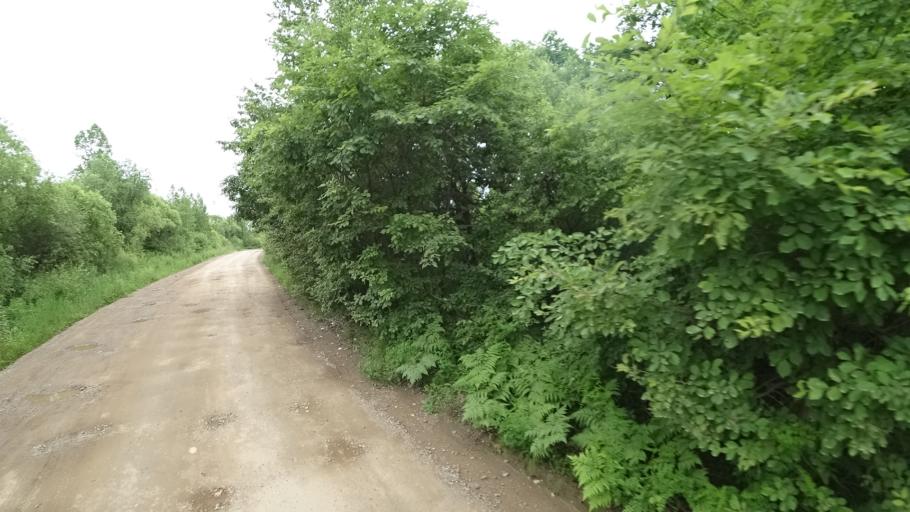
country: RU
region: Primorskiy
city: Arsen'yev
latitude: 44.1926
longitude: 133.3104
